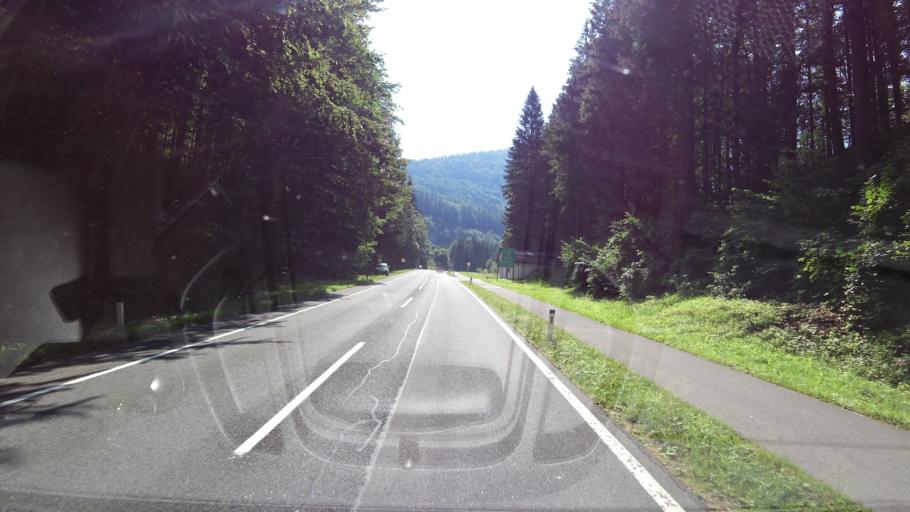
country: AT
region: Salzburg
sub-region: Politischer Bezirk Hallein
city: Scheffau am Tennengebirge
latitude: 47.5785
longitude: 13.1909
